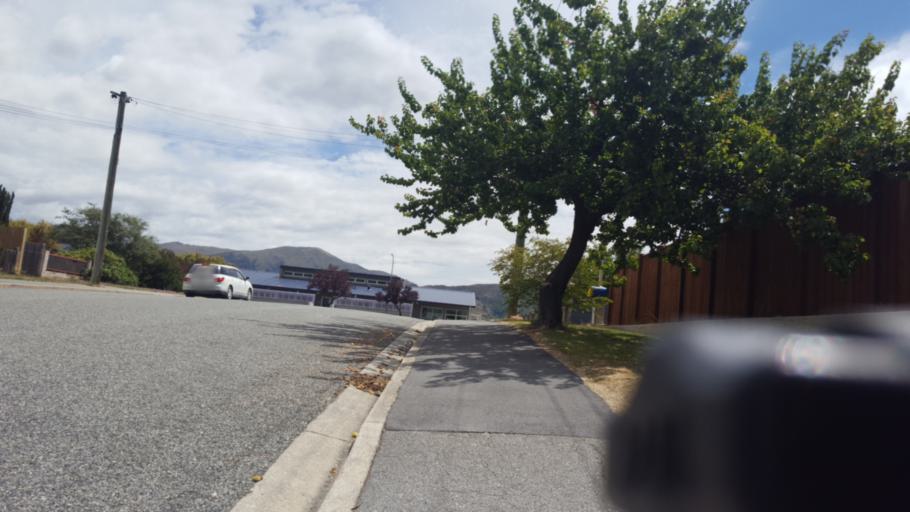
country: NZ
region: Otago
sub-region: Queenstown-Lakes District
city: Wanaka
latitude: -45.0445
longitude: 169.2055
